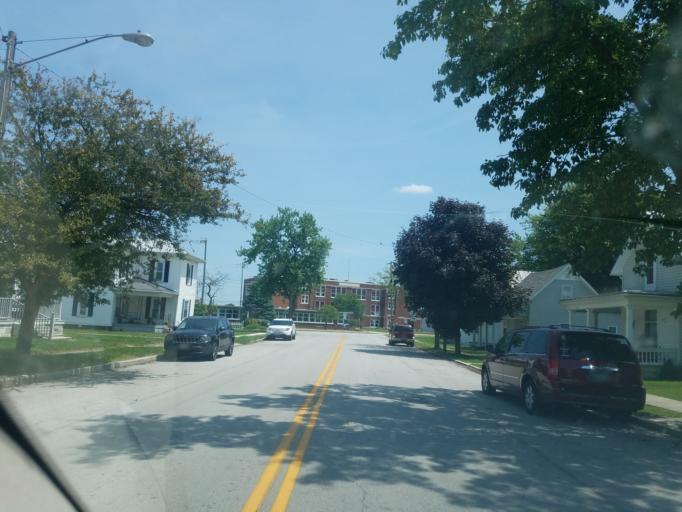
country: US
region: Ohio
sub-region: Wyandot County
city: Carey
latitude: 40.9746
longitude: -83.4776
